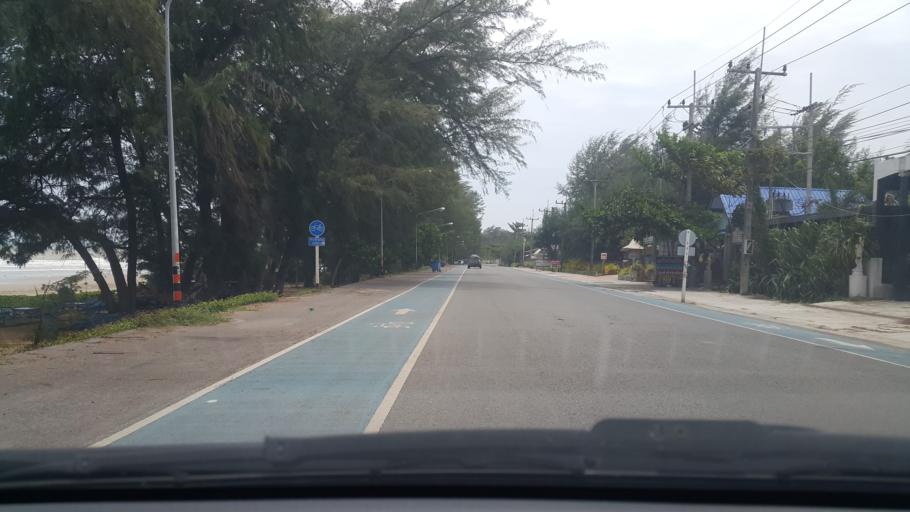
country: TH
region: Rayong
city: Rayong
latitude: 12.6090
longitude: 101.3890
